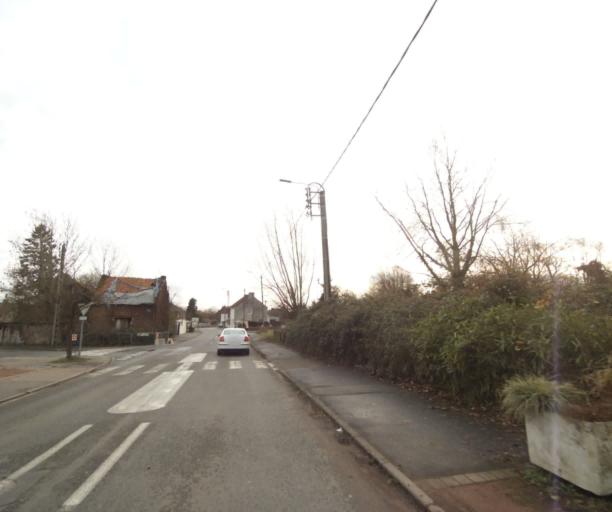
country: FR
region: Nord-Pas-de-Calais
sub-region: Departement du Nord
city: Vieux-Conde
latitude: 50.4664
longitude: 3.5472
